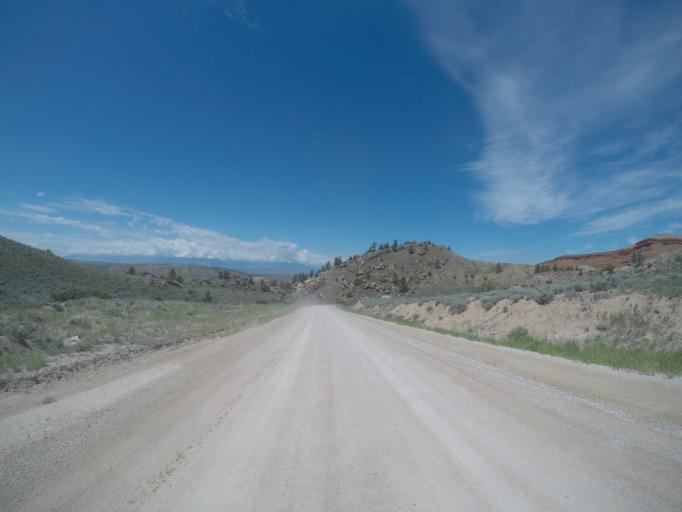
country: US
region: Montana
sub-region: Carbon County
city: Red Lodge
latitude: 45.2101
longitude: -108.8078
